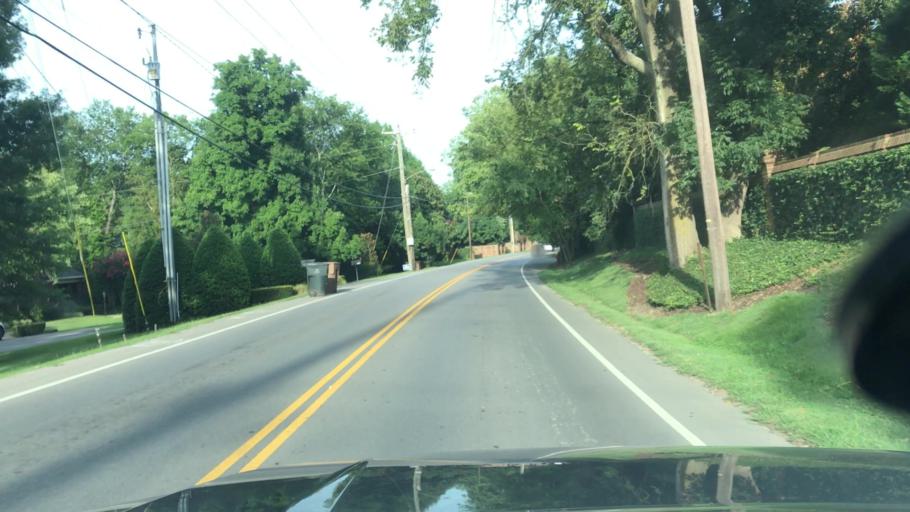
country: US
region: Tennessee
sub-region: Davidson County
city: Belle Meade
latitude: 36.0927
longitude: -86.8392
